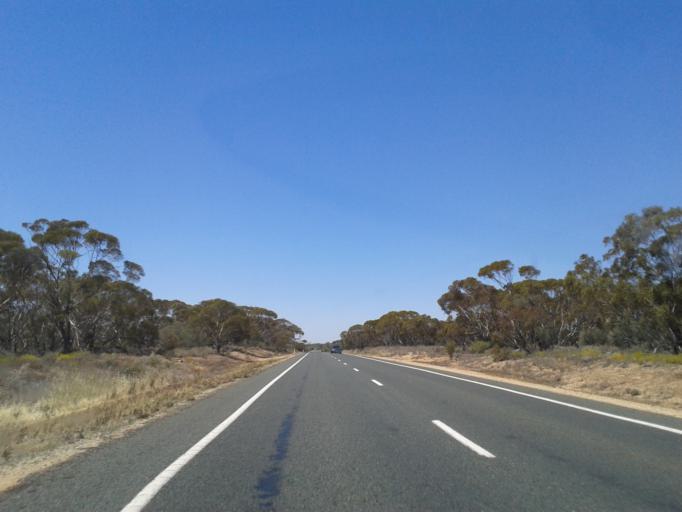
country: AU
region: New South Wales
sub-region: Wentworth
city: Gol Gol
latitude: -34.5340
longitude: 142.6336
